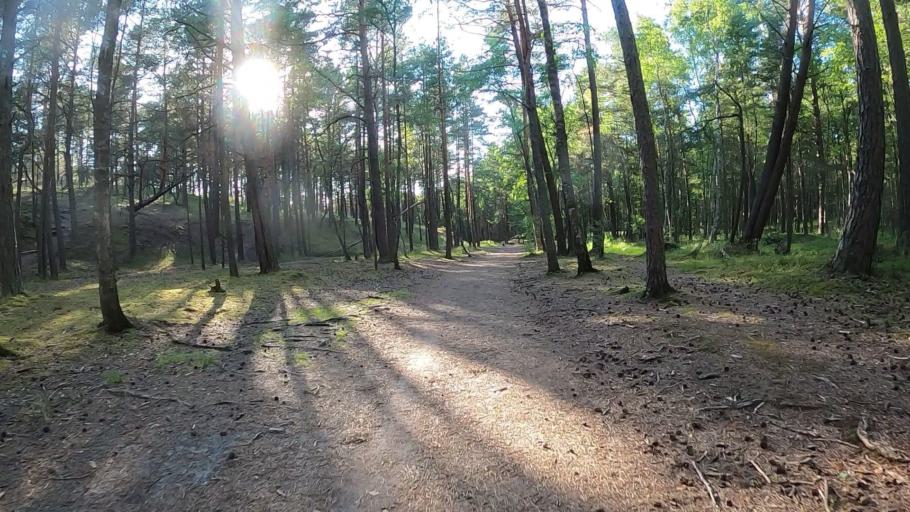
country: LV
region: Carnikava
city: Carnikava
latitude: 57.1378
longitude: 24.2449
